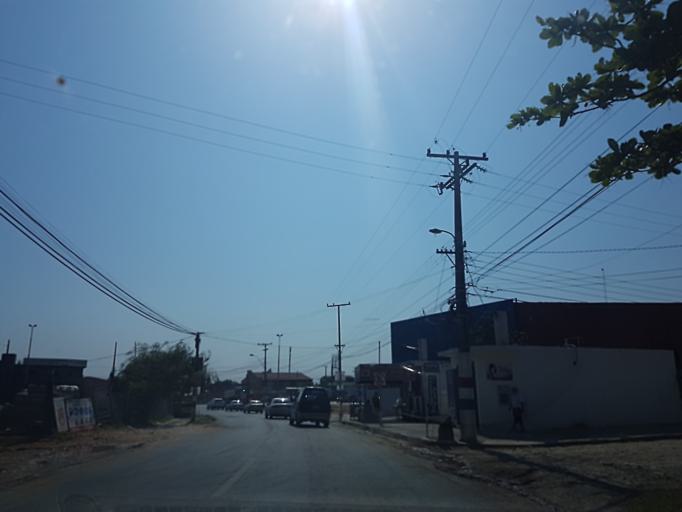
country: PY
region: Central
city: Colonia Mariano Roque Alonso
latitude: -25.2135
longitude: -57.5282
